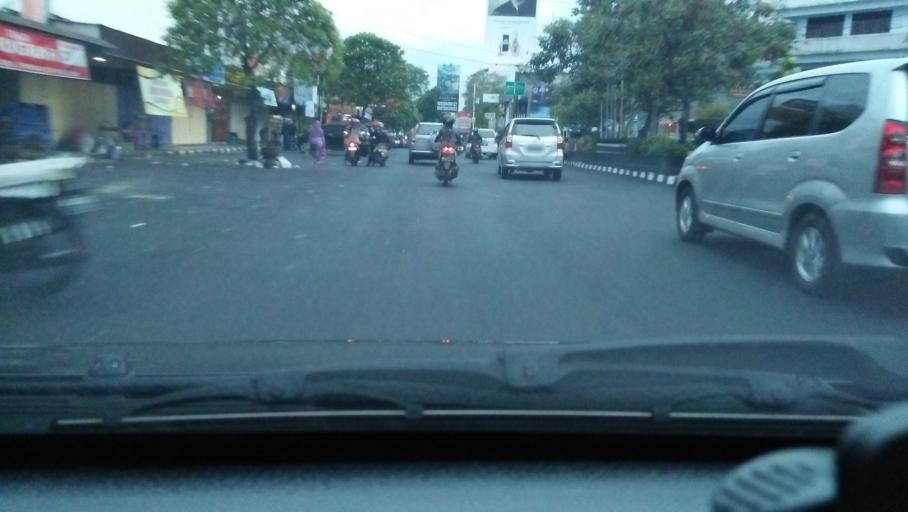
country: ID
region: Central Java
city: Magelang
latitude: -7.4863
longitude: 110.2212
